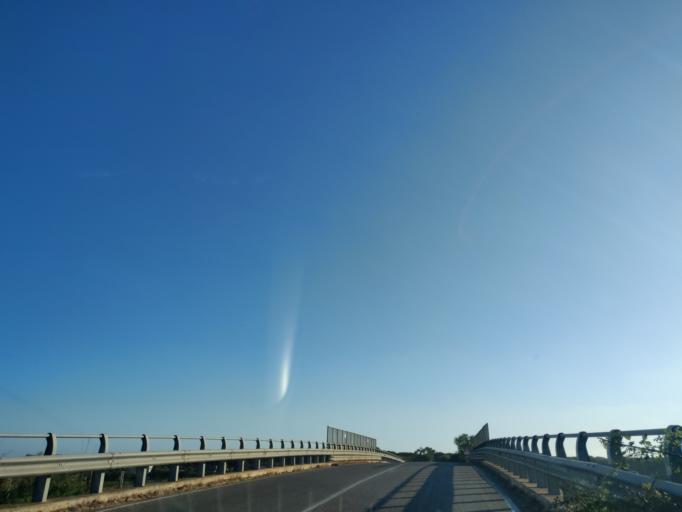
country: IT
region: Latium
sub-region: Provincia di Viterbo
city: Montalto di Castro
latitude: 42.2993
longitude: 11.6502
